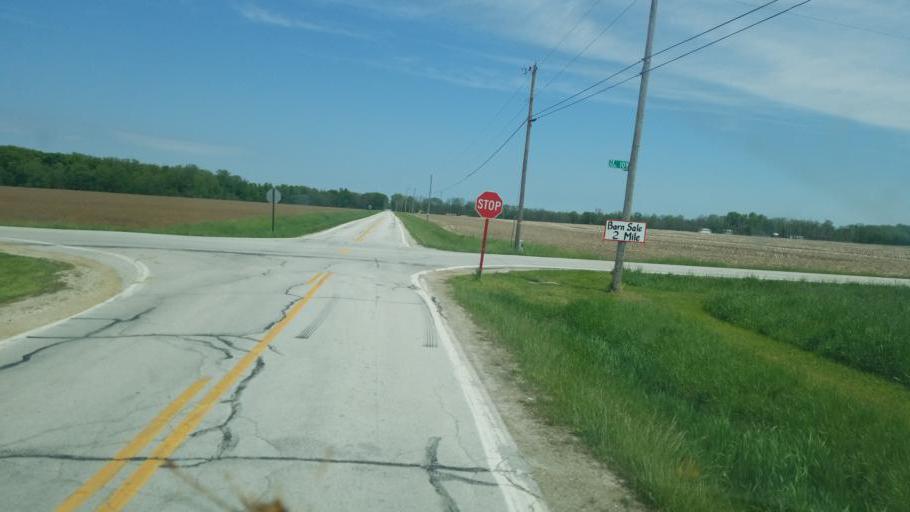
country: US
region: Ohio
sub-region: Sandusky County
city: Stony Prairie
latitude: 41.4140
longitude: -83.2019
